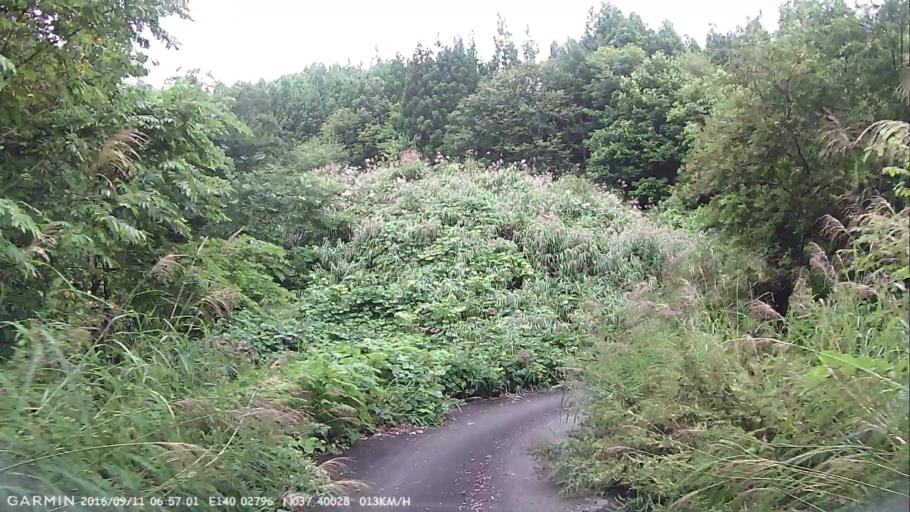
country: JP
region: Fukushima
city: Inawashiro
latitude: 37.4003
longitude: 140.0279
